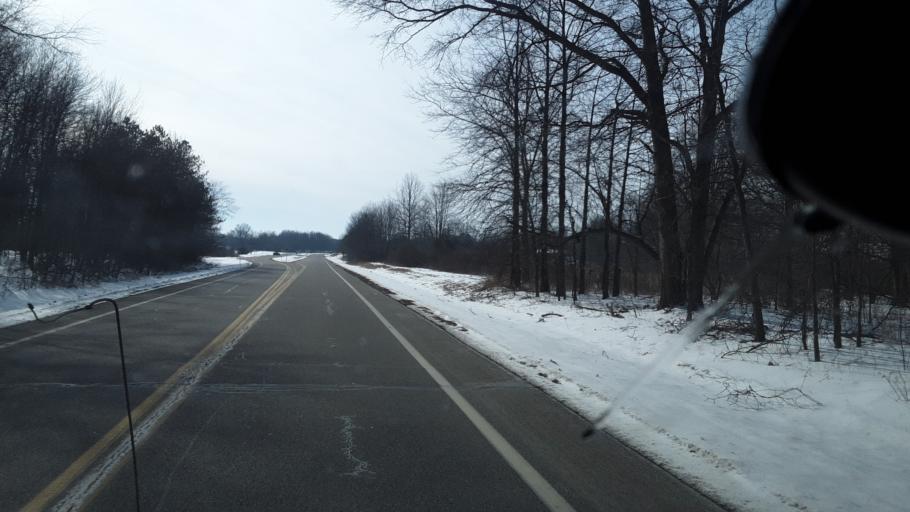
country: US
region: Ohio
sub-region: Portage County
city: Ravenna
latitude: 41.0323
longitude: -81.2087
